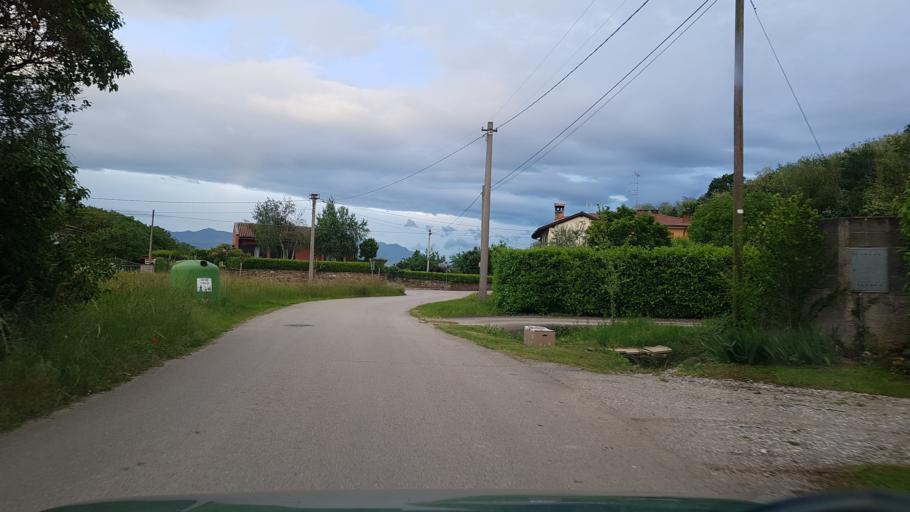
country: IT
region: Friuli Venezia Giulia
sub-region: Provincia di Gorizia
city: Farra d'Isonzo
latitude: 45.9115
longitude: 13.5328
